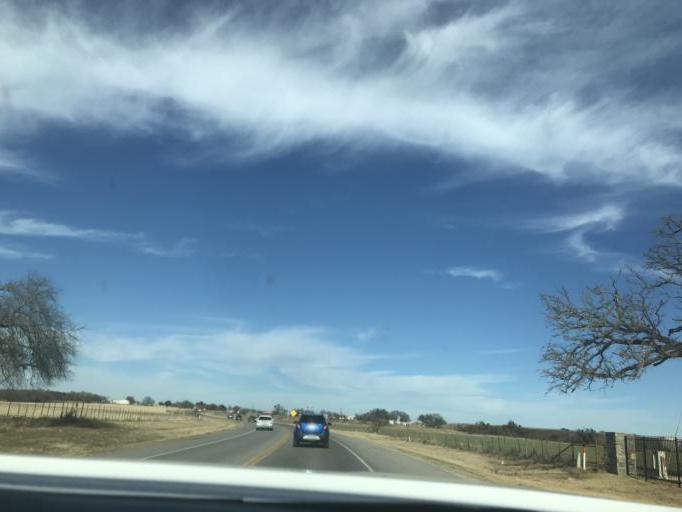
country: US
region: Texas
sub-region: Erath County
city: Stephenville
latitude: 32.2379
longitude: -98.1994
